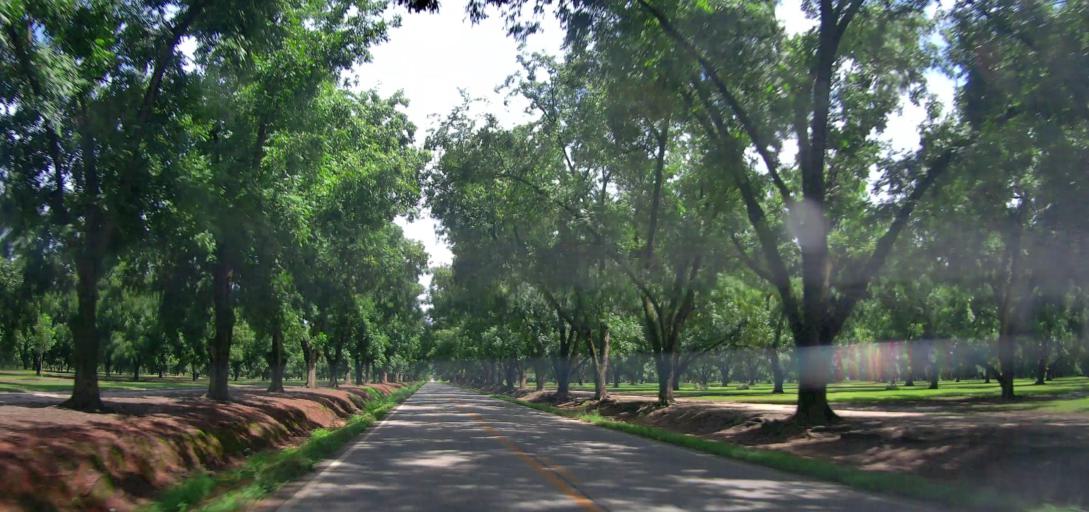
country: US
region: Georgia
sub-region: Houston County
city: Perry
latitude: 32.5212
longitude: -83.7914
